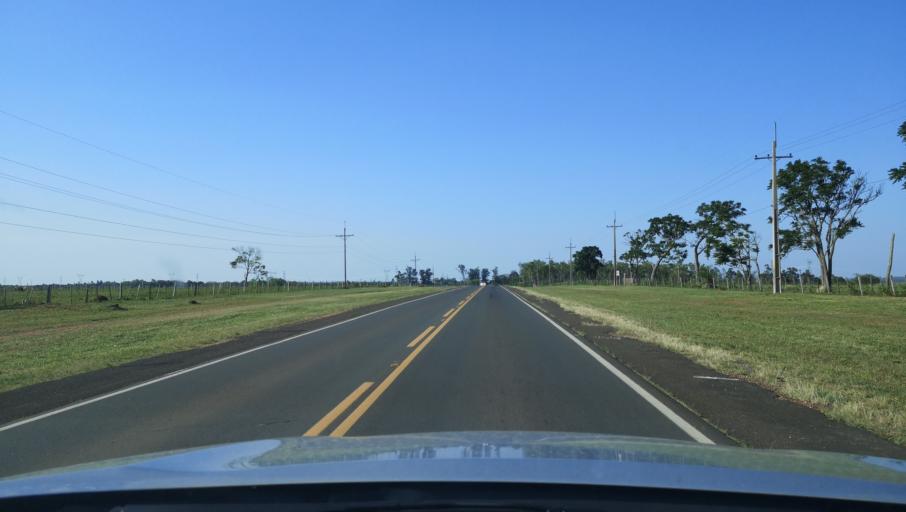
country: PY
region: Misiones
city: Santa Maria
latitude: -26.8127
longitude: -57.0226
